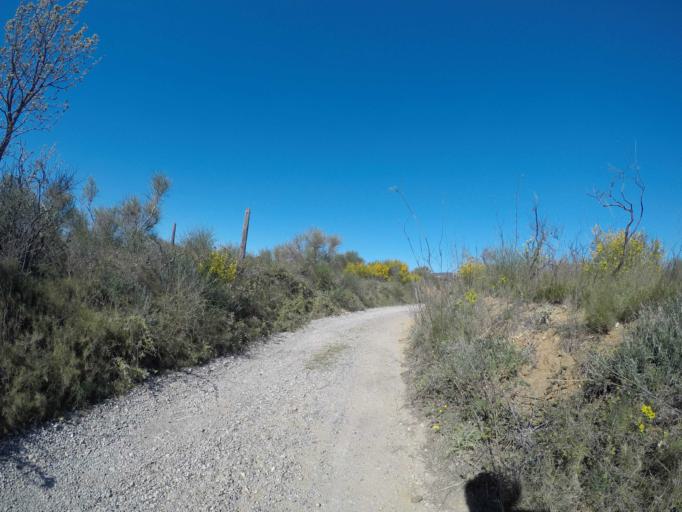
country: FR
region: Languedoc-Roussillon
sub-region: Departement des Pyrenees-Orientales
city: Millas
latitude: 42.7059
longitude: 2.6734
